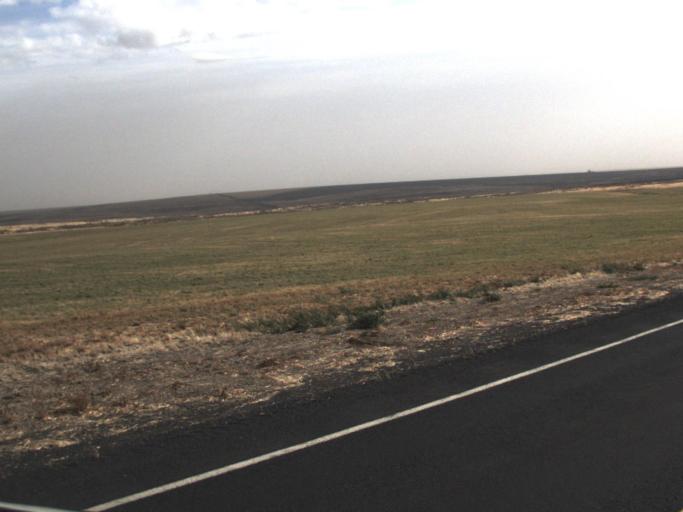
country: US
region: Washington
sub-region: Okanogan County
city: Coulee Dam
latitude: 47.4808
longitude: -118.7849
